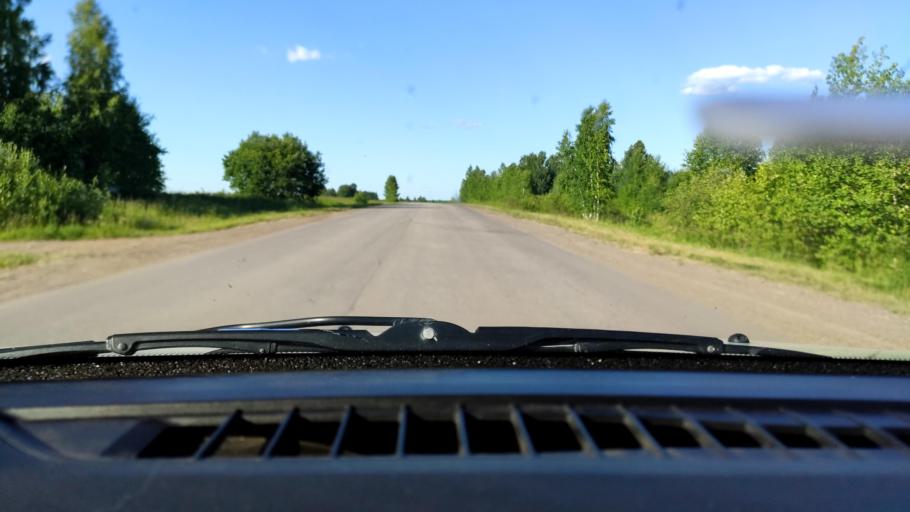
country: RU
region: Perm
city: Orda
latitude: 57.1858
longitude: 56.8470
